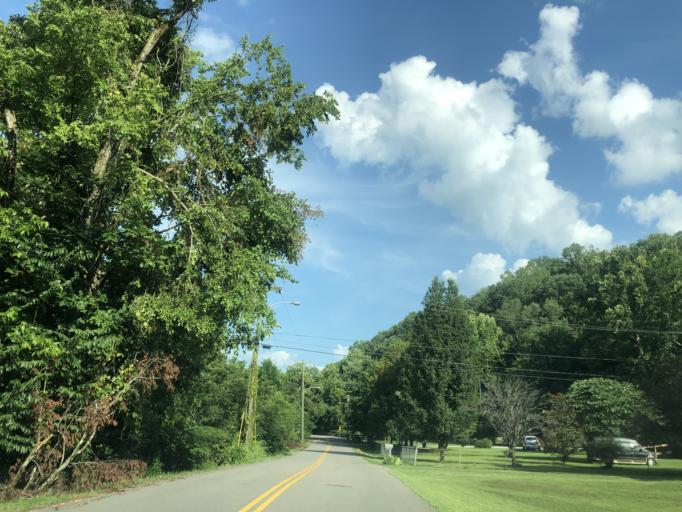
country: US
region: Tennessee
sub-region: Davidson County
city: Nashville
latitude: 36.2483
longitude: -86.8384
